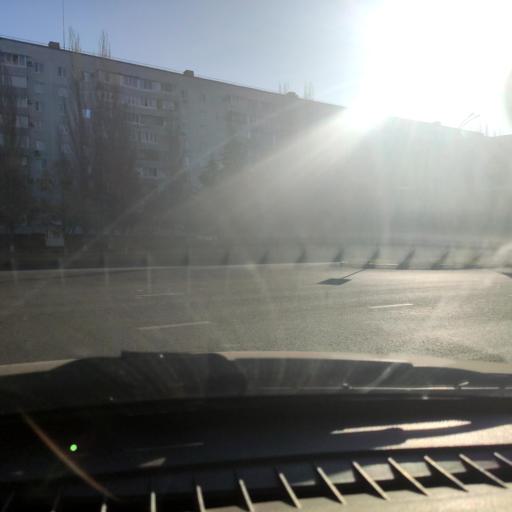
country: RU
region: Samara
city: Tol'yatti
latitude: 53.5096
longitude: 49.2923
